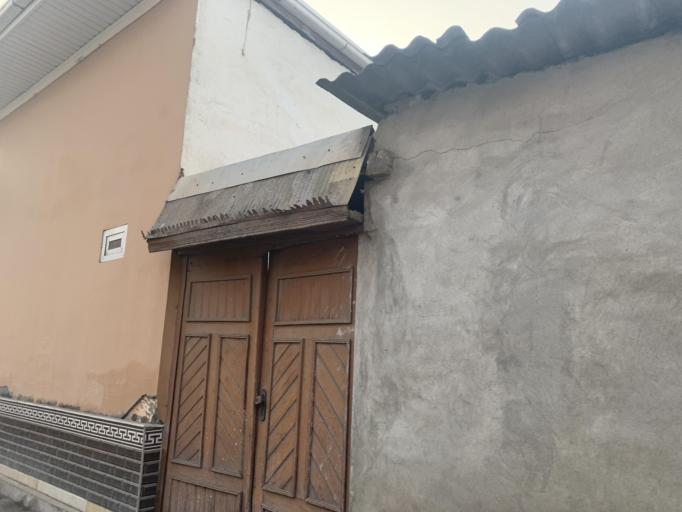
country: UZ
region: Fergana
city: Qo`qon
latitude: 40.5384
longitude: 70.9294
